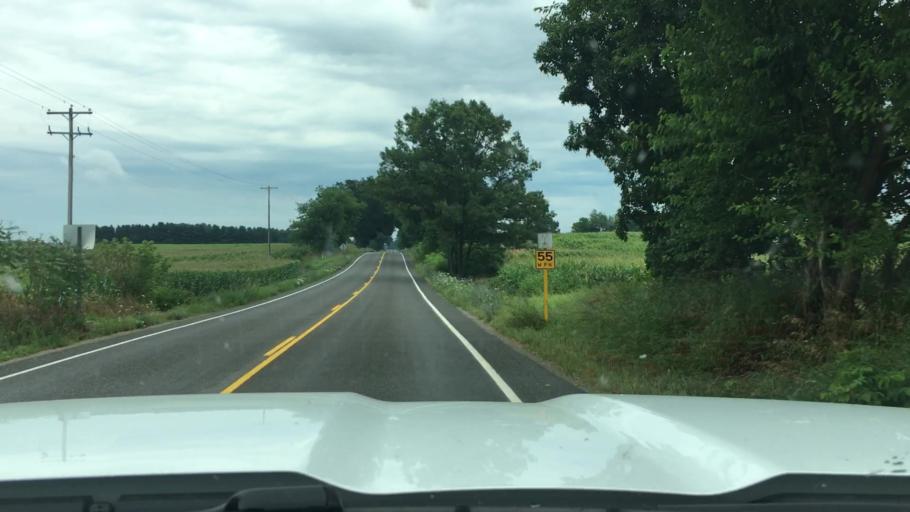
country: US
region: Michigan
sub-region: Barry County
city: Stony Point
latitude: 42.4282
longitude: -85.4830
